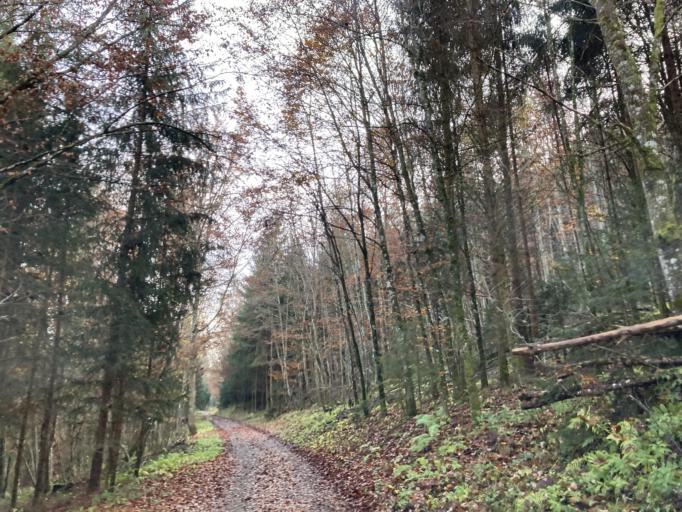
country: DE
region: Baden-Wuerttemberg
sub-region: Regierungsbezirk Stuttgart
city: Bondorf
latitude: 48.4670
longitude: 8.8501
